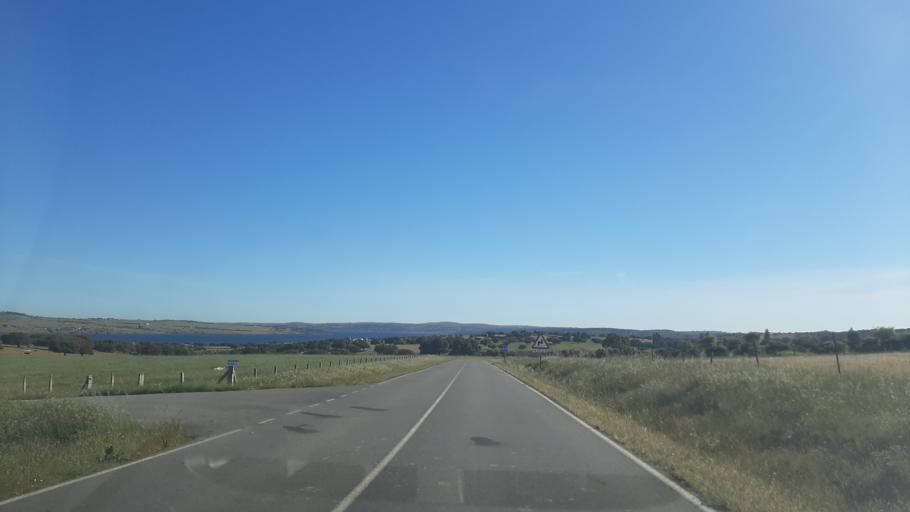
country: ES
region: Castille and Leon
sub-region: Provincia de Salamanca
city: Salvatierra de Tormes
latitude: 40.5504
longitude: -5.5938
